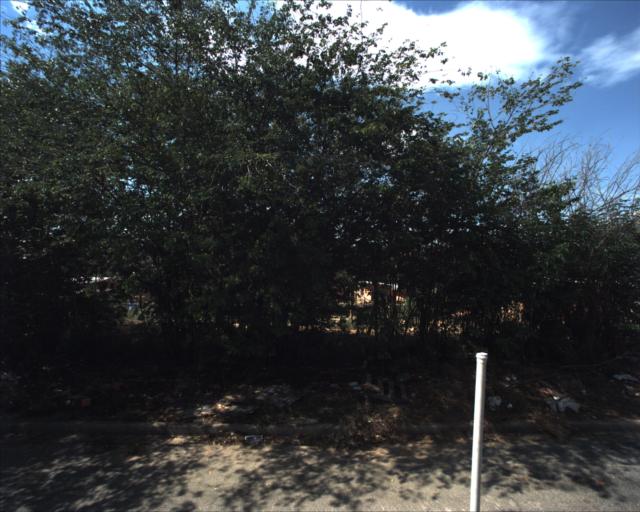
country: BR
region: Sao Paulo
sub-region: Sorocaba
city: Sorocaba
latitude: -23.4742
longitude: -47.5110
